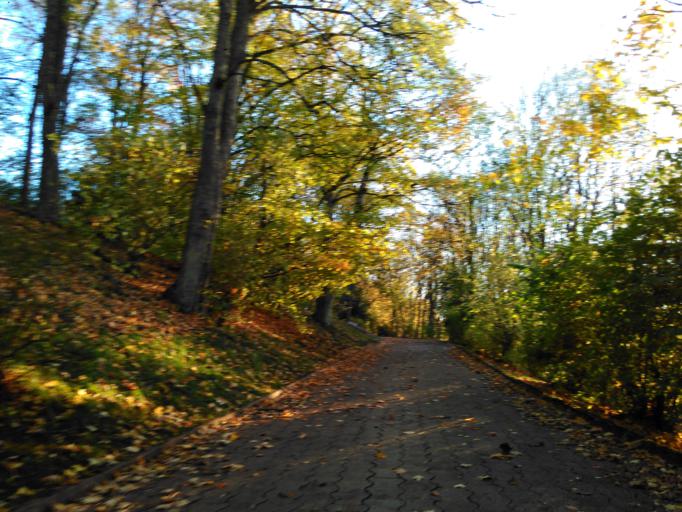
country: LU
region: Luxembourg
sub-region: Canton d'Esch-sur-Alzette
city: Esch-sur-Alzette
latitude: 49.4915
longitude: 5.9846
